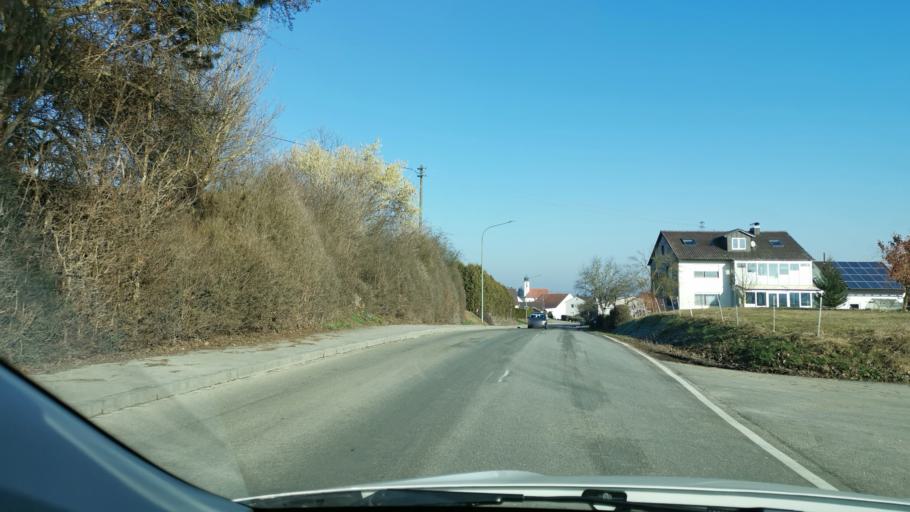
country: DE
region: Bavaria
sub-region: Swabia
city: Holzheim
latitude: 48.6074
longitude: 10.9479
